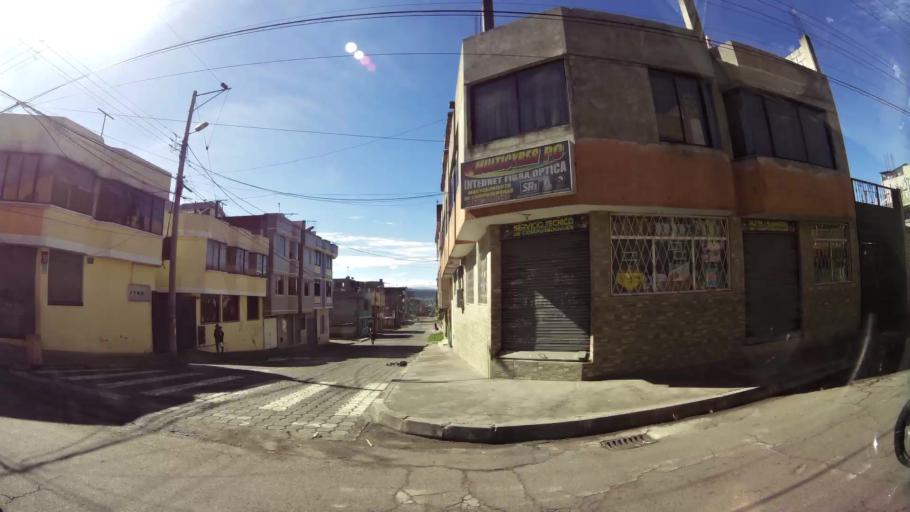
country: EC
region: Pichincha
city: Quito
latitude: -0.2952
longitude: -78.5686
